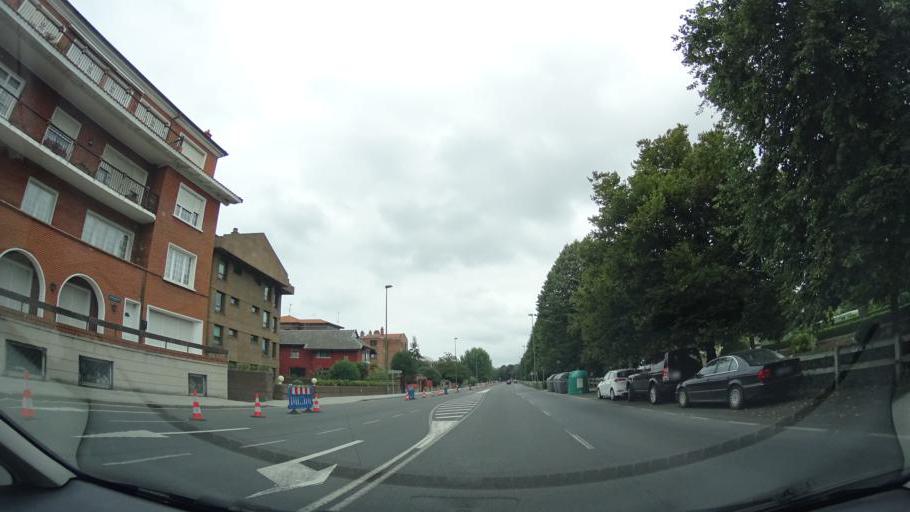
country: ES
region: Basque Country
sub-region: Bizkaia
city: Portugalete
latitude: 43.3292
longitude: -3.0138
